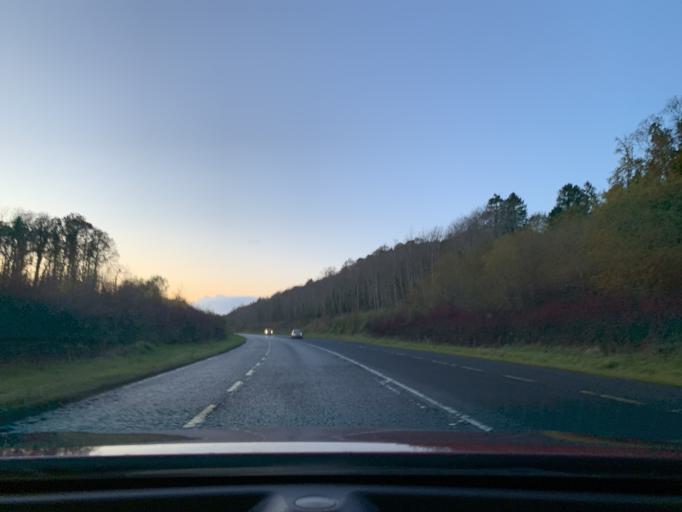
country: IE
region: Connaught
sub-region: County Leitrim
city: Carrick-on-Shannon
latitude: 53.9360
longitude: -8.0113
